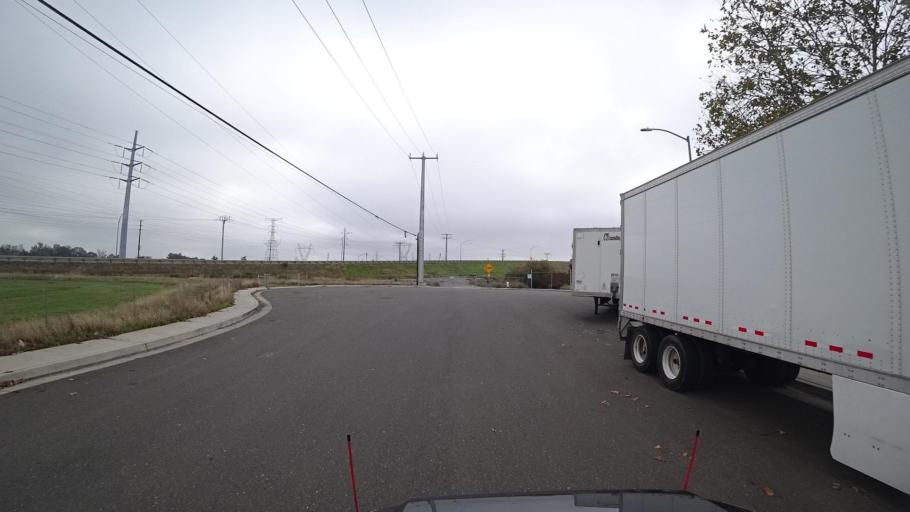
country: US
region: California
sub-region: Sacramento County
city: Elk Grove
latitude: 38.3835
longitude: -121.3529
